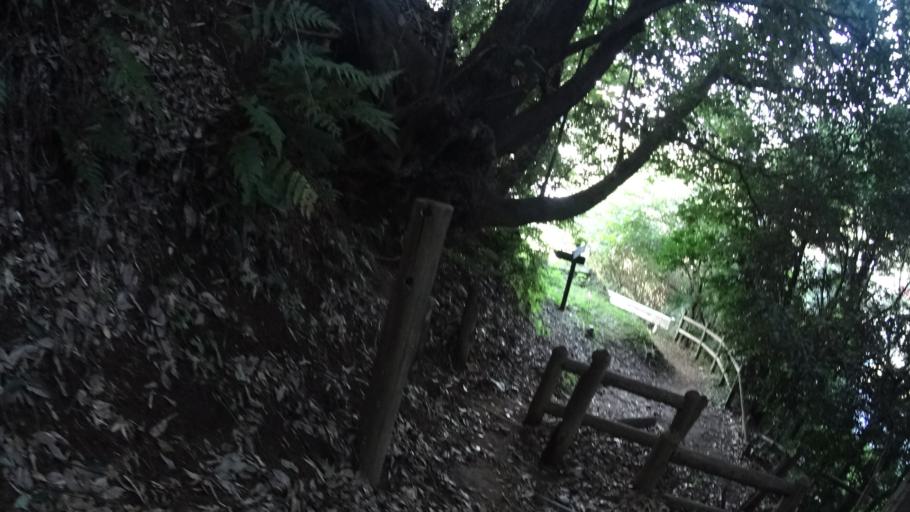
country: JP
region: Kanagawa
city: Zushi
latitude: 35.3593
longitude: 139.6039
